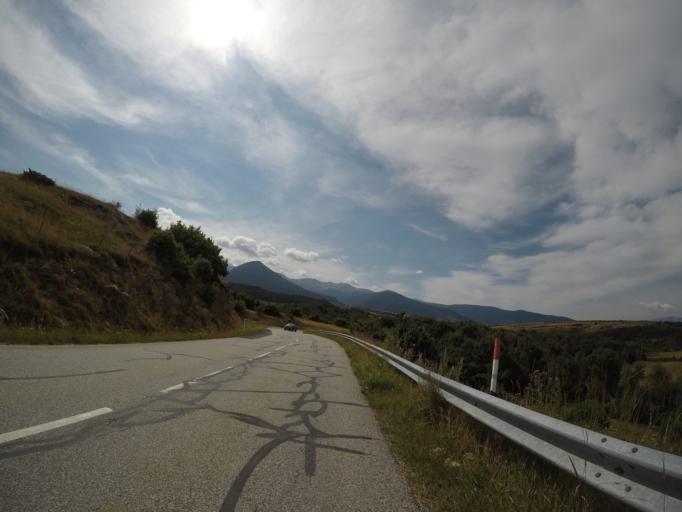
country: ES
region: Catalonia
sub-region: Provincia de Girona
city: Llivia
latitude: 42.4872
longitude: 2.0528
